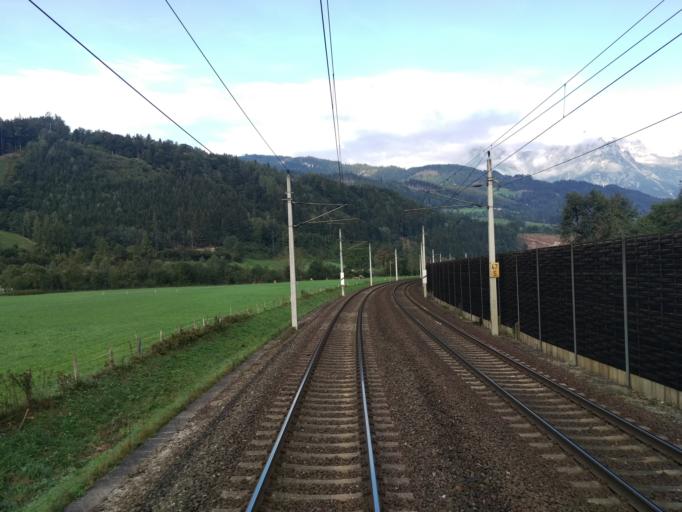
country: AT
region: Salzburg
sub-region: Politischer Bezirk Sankt Johann im Pongau
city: Pfarrwerfen
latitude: 47.4550
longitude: 13.2062
